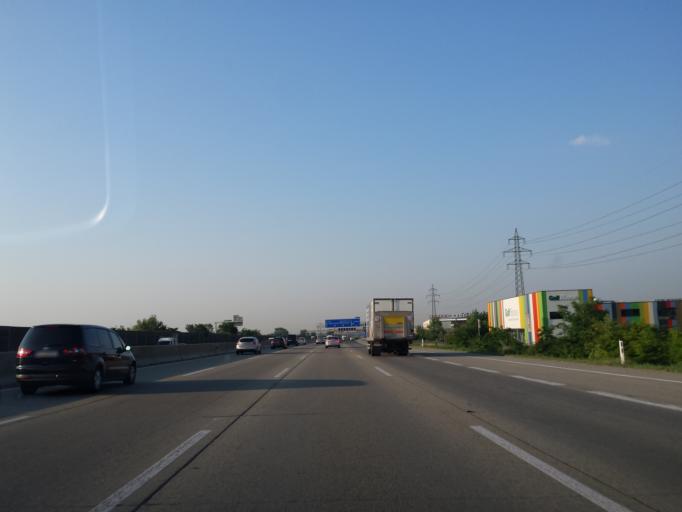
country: AT
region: Lower Austria
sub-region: Politischer Bezirk Modling
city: Biedermannsdorf
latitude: 48.0742
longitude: 16.3376
